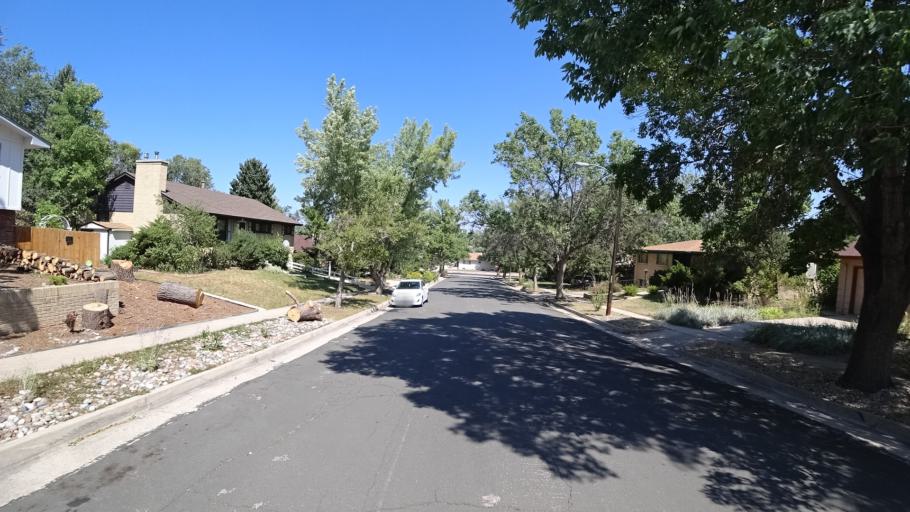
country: US
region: Colorado
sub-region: El Paso County
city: Colorado Springs
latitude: 38.8492
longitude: -104.7990
